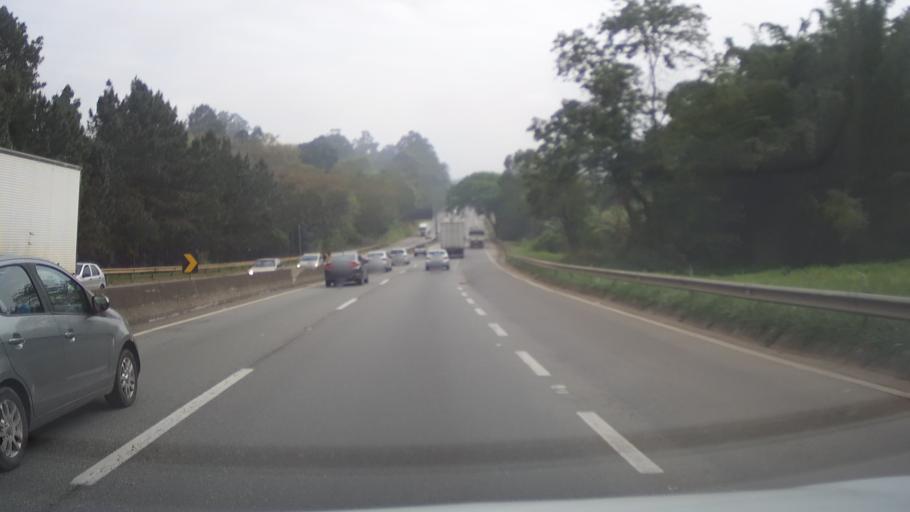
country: BR
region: Sao Paulo
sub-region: Atibaia
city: Atibaia
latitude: -23.0920
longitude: -46.5728
